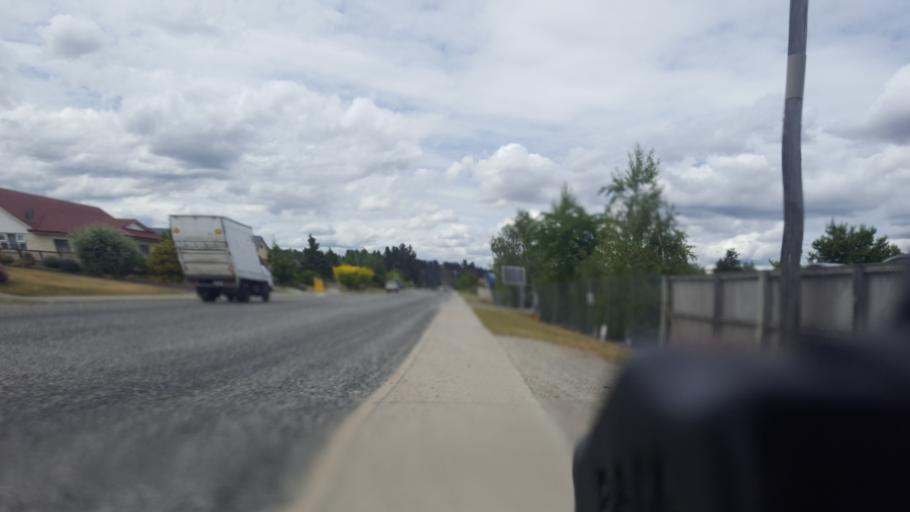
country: NZ
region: Otago
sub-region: Queenstown-Lakes District
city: Wanaka
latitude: -45.2466
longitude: 169.3753
